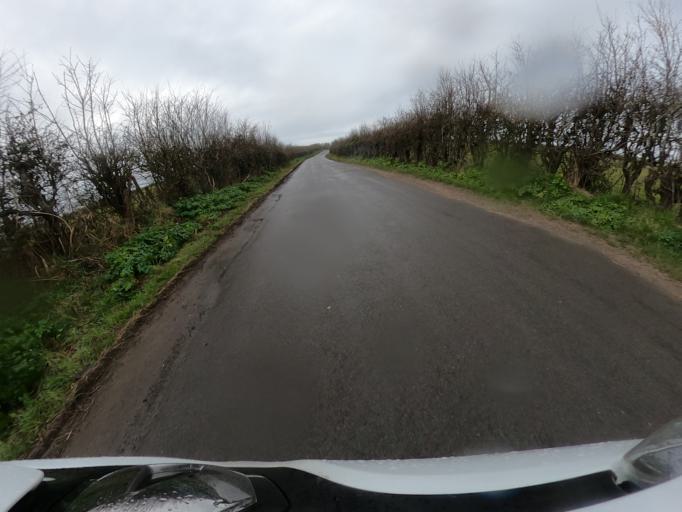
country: IM
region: Ramsey
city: Ramsey
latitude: 54.3800
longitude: -4.4595
